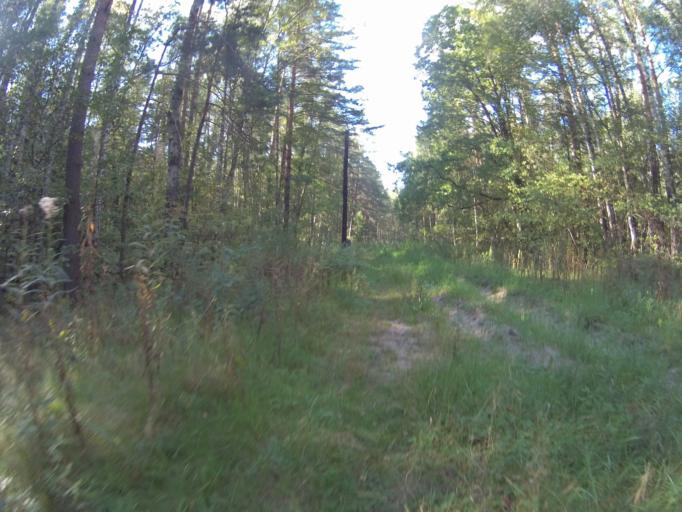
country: RU
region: Vladimir
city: Kommunar
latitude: 56.0747
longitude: 40.4452
